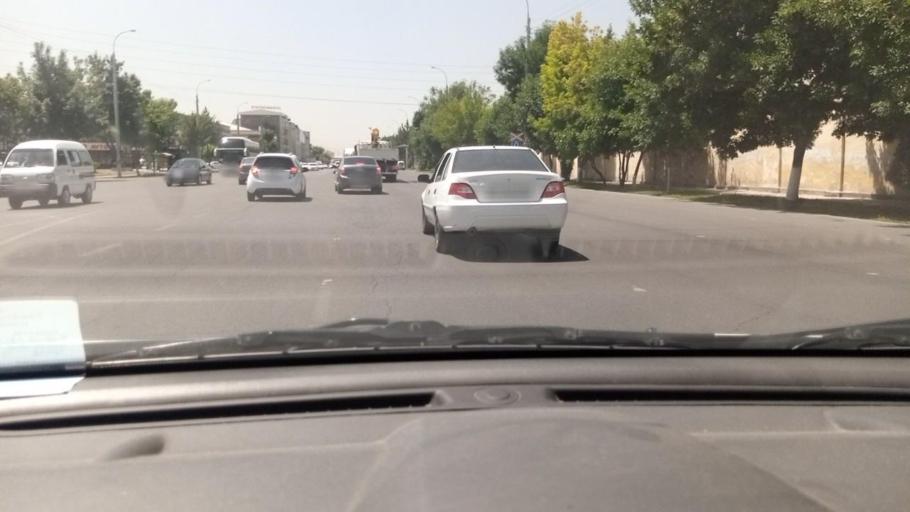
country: UZ
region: Toshkent Shahri
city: Tashkent
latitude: 41.2640
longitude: 69.2353
